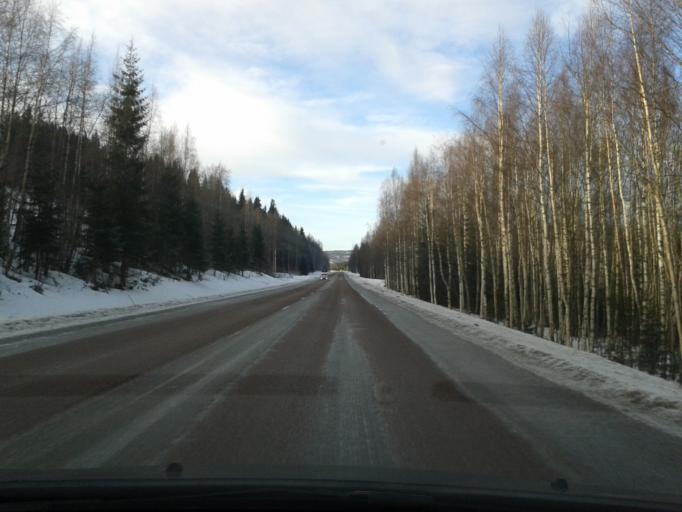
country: SE
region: Vaesternorrland
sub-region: OErnskoeldsviks Kommun
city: Bjasta
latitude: 63.3498
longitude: 18.4954
